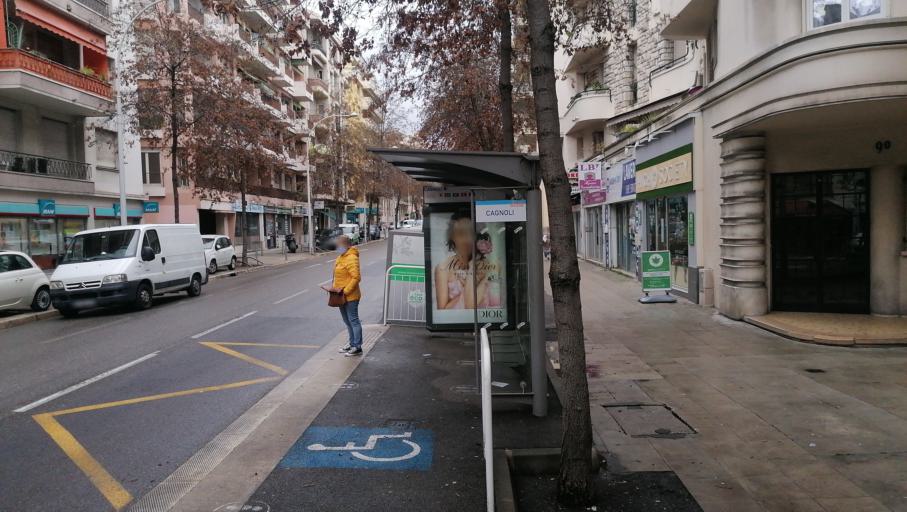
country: FR
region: Provence-Alpes-Cote d'Azur
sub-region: Departement des Alpes-Maritimes
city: Nice
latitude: 43.7175
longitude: 7.2530
